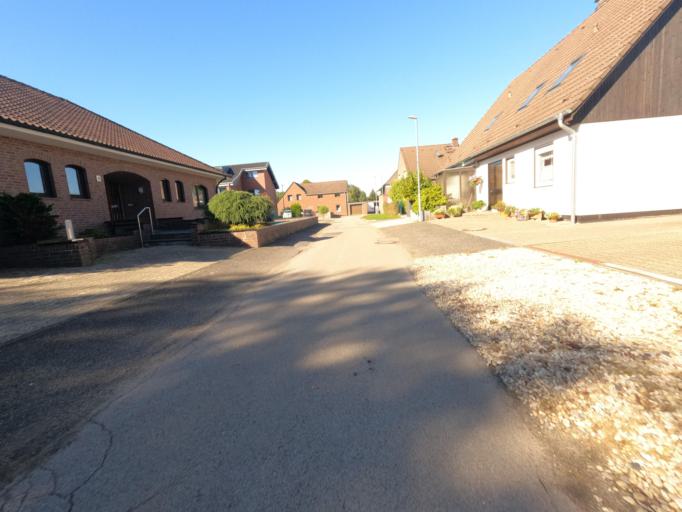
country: DE
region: North Rhine-Westphalia
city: Erkelenz
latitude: 51.0740
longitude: 6.3434
